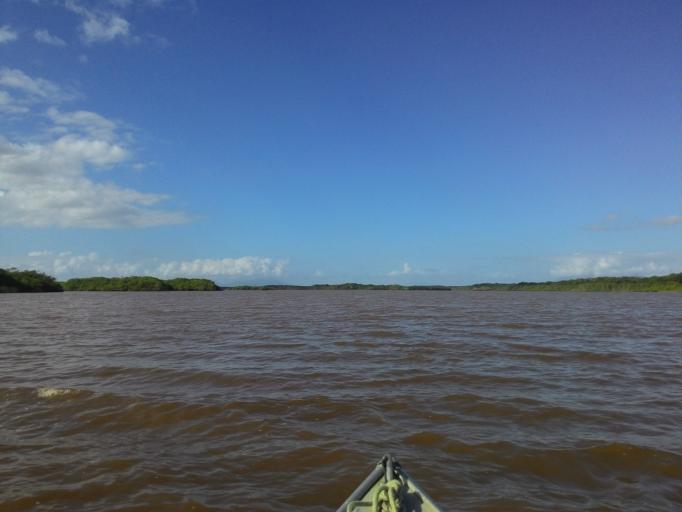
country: BR
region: Sao Paulo
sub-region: Pariquera-Acu
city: Pariquera Acu
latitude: -24.8572
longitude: -47.7638
